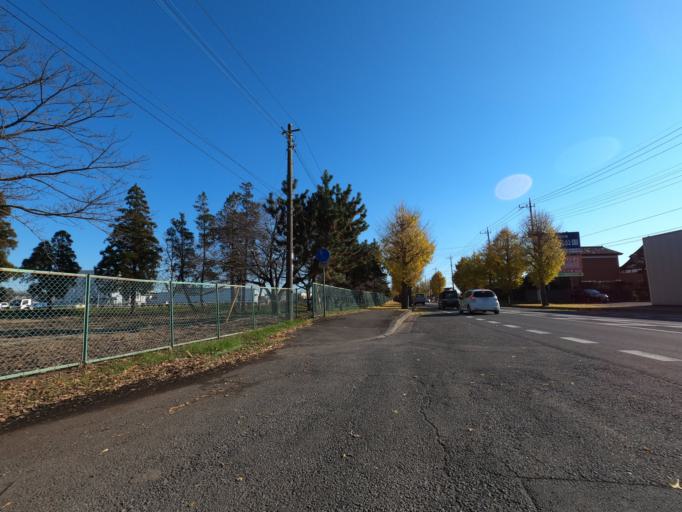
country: JP
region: Ibaraki
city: Moriya
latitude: 35.9576
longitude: 139.9773
